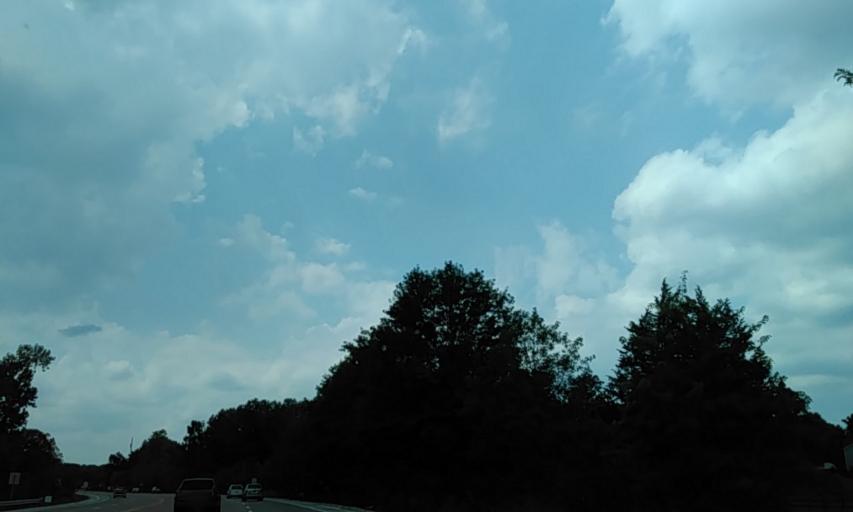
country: US
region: Missouri
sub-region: Saint Louis County
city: Town and Country
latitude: 38.5801
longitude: -90.4597
